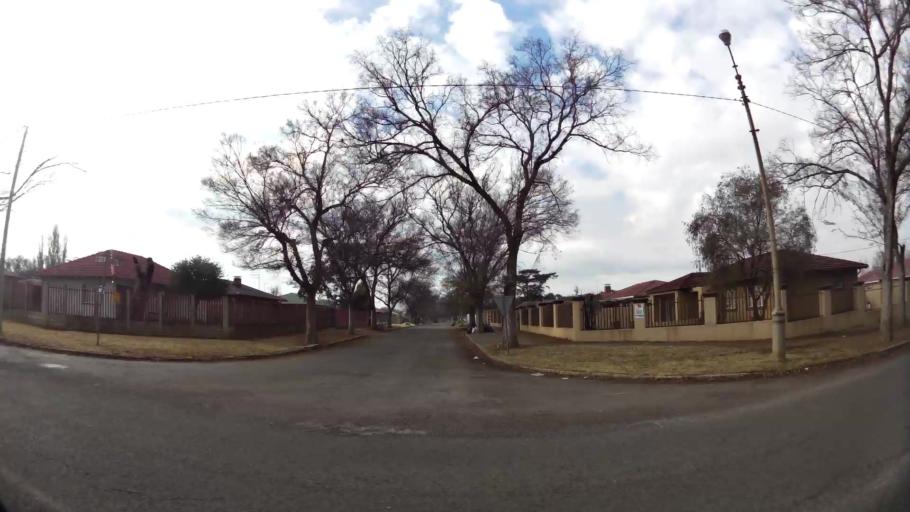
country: ZA
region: Gauteng
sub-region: Sedibeng District Municipality
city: Vanderbijlpark
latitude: -26.6933
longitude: 27.8149
